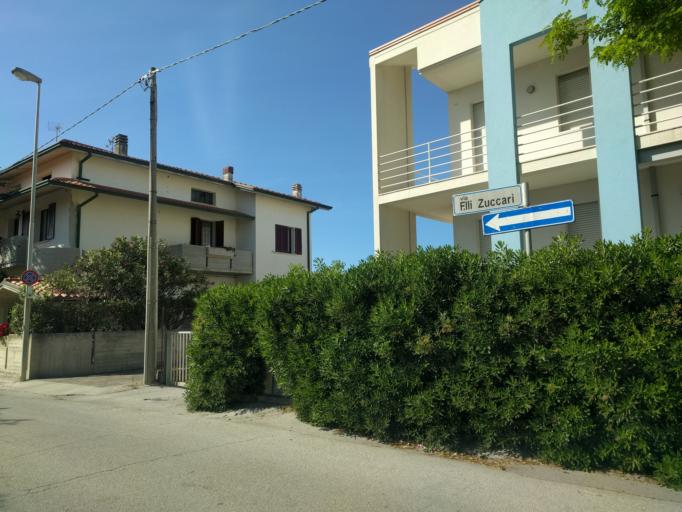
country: IT
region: The Marches
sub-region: Provincia di Pesaro e Urbino
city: Fano
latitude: 43.8356
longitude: 13.0424
